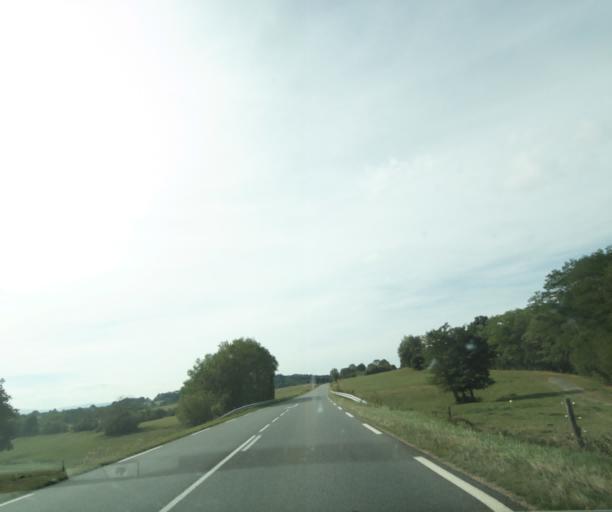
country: FR
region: Auvergne
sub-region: Departement de l'Allier
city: Le Donjon
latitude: 46.2758
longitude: 3.7390
